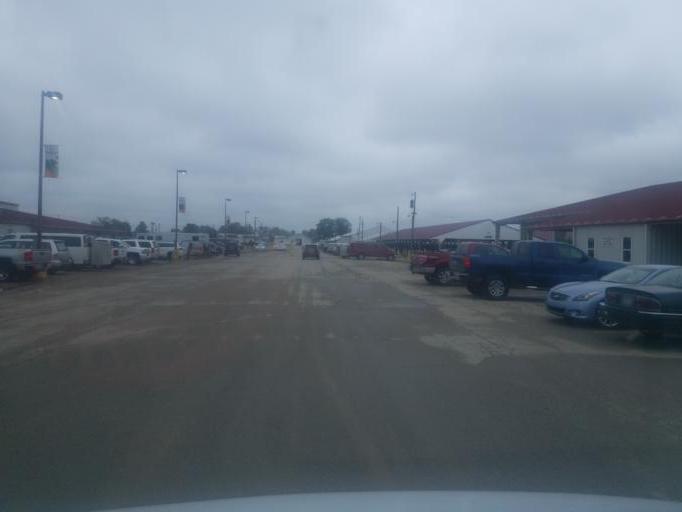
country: US
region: Ohio
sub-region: Clark County
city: Springfield
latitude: 39.8954
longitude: -83.7327
